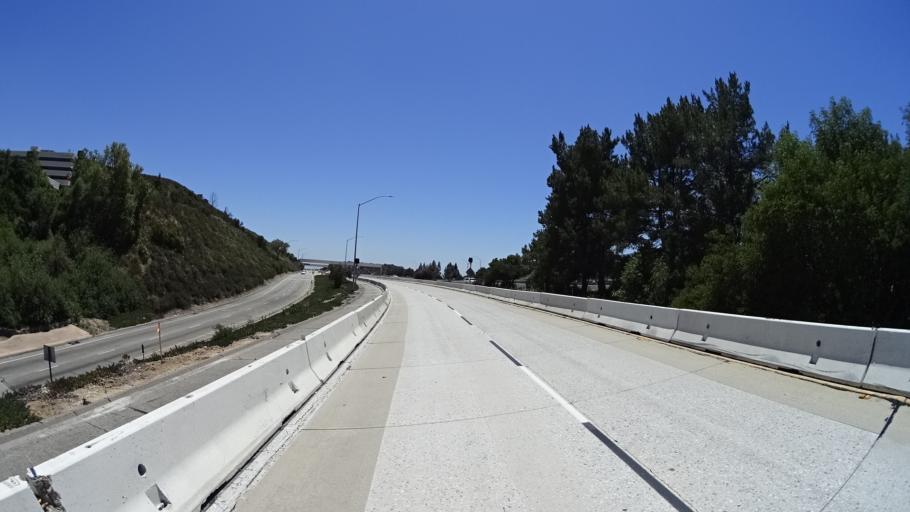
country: US
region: California
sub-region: Los Angeles County
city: La Canada Flintridge
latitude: 34.2050
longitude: -118.2178
